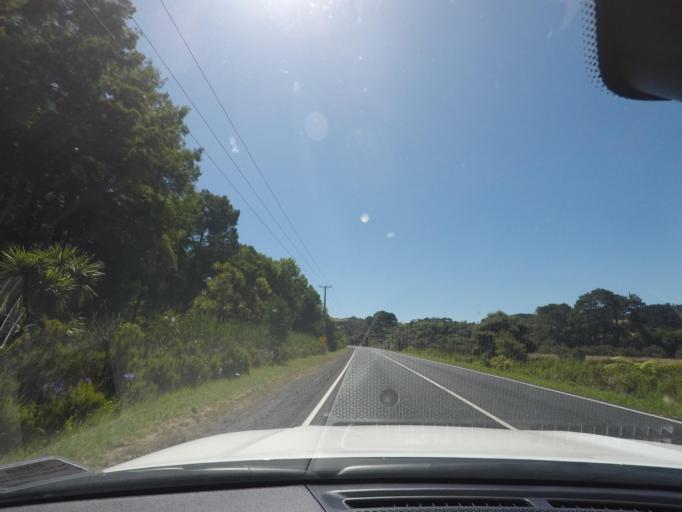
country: NZ
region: Auckland
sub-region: Auckland
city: Parakai
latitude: -36.5862
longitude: 174.3354
